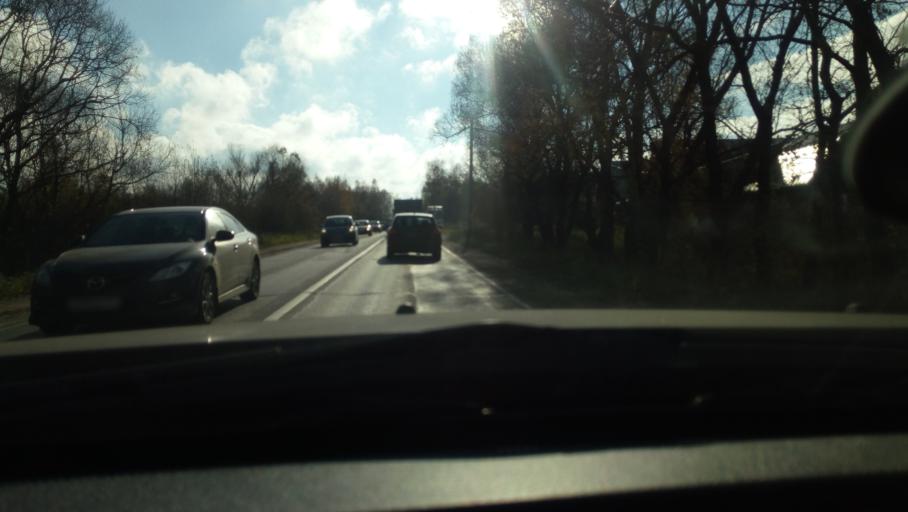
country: RU
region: Moskovskaya
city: Fryazevo
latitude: 55.7224
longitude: 38.4663
